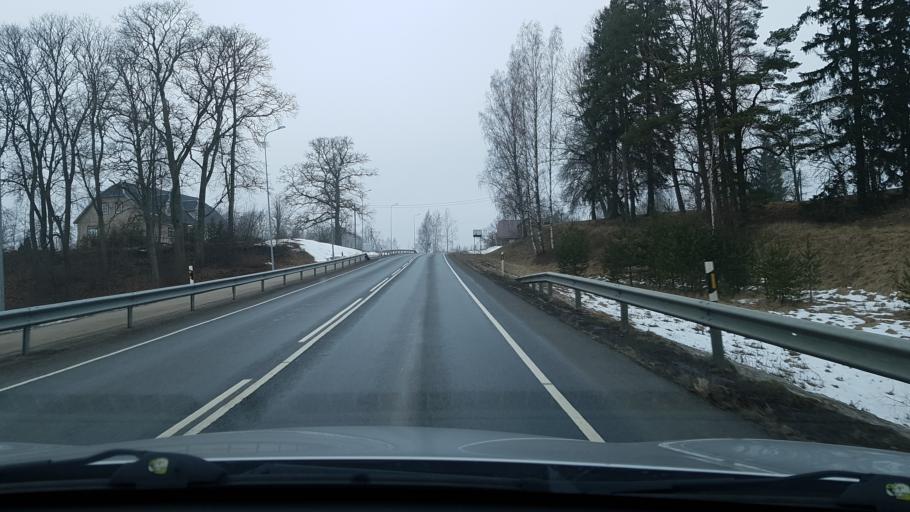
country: EE
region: Valgamaa
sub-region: Torva linn
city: Torva
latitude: 58.2290
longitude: 25.8843
